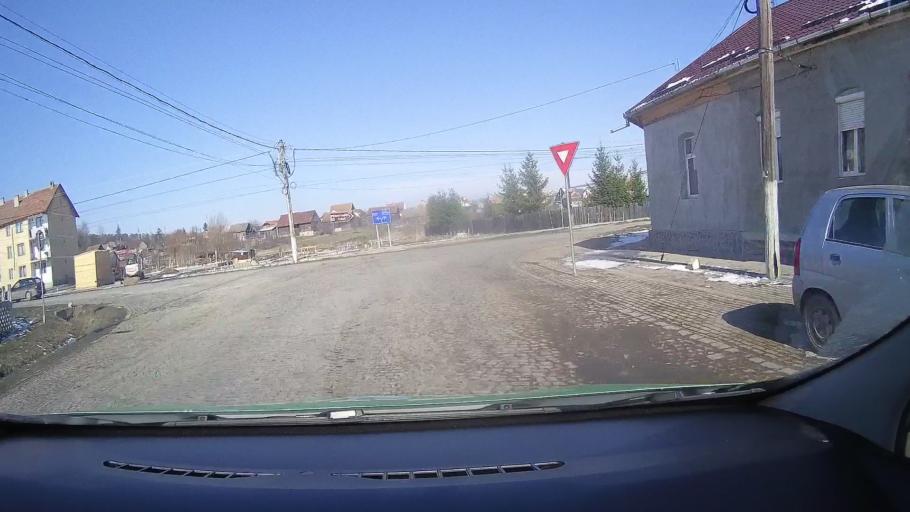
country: RO
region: Brasov
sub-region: Comuna Homorod
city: Homorod
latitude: 46.0389
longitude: 25.2746
